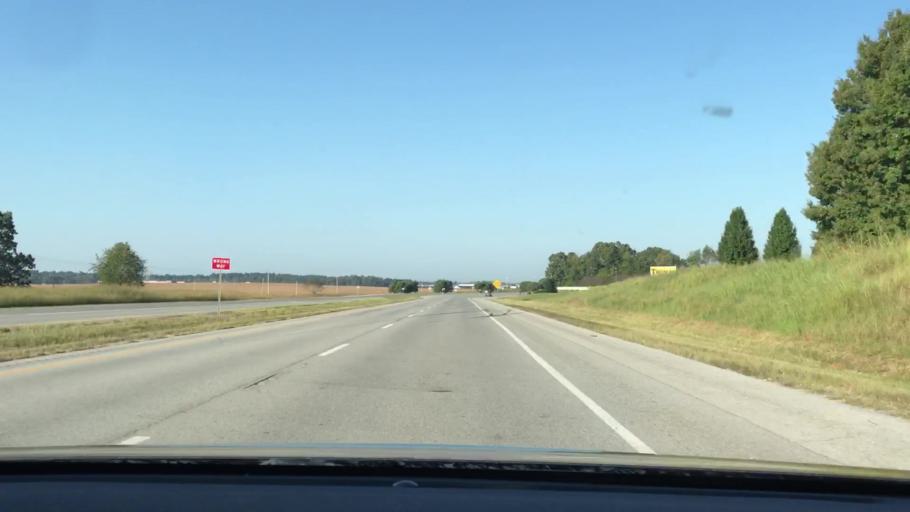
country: US
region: Kentucky
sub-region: Trigg County
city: Cadiz
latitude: 36.8682
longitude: -87.7726
